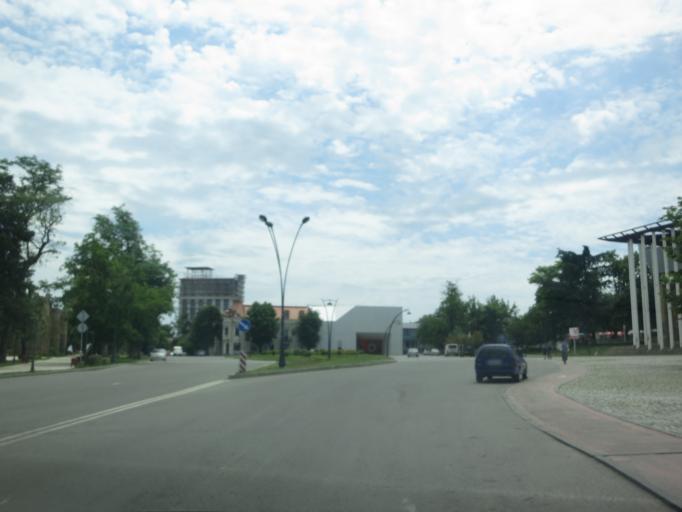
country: GE
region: Kakheti
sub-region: Telavi
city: Telavi
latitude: 41.9181
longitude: 45.4732
